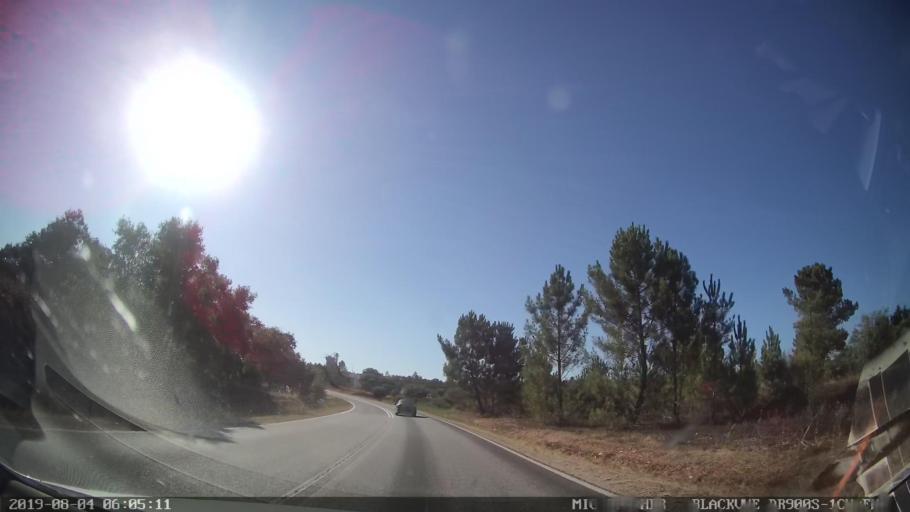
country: PT
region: Santarem
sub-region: Abrantes
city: Alferrarede
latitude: 39.4748
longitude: -8.0729
